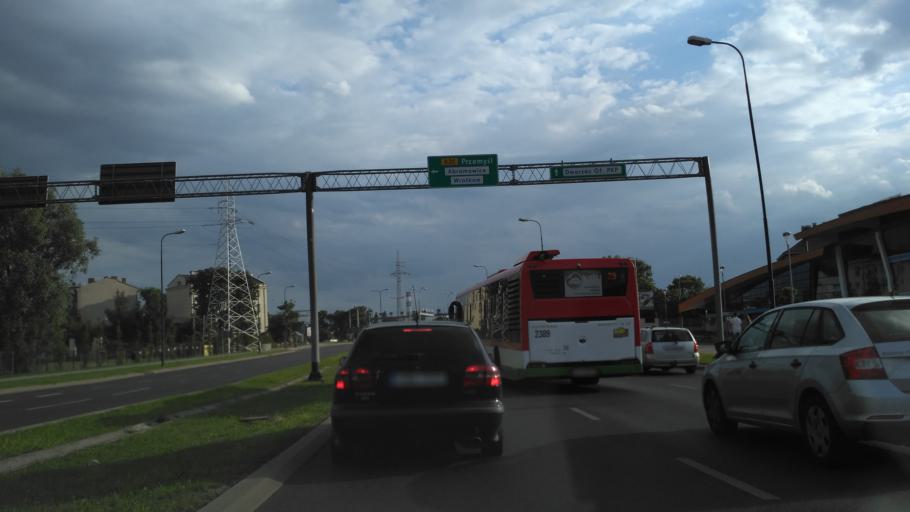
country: PL
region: Lublin Voivodeship
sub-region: Powiat lubelski
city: Lublin
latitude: 51.2369
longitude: 22.5698
